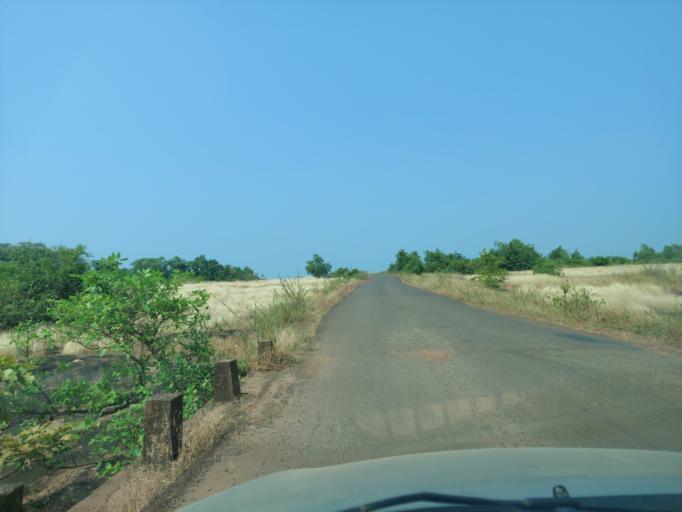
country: IN
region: Maharashtra
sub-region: Sindhudurg
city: Malvan
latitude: 15.9969
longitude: 73.5181
